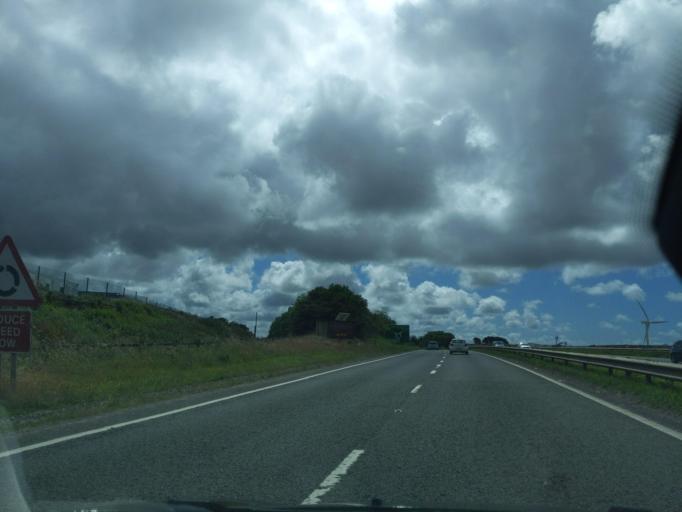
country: GB
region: England
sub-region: Cornwall
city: Newquay
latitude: 50.3496
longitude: -5.0337
